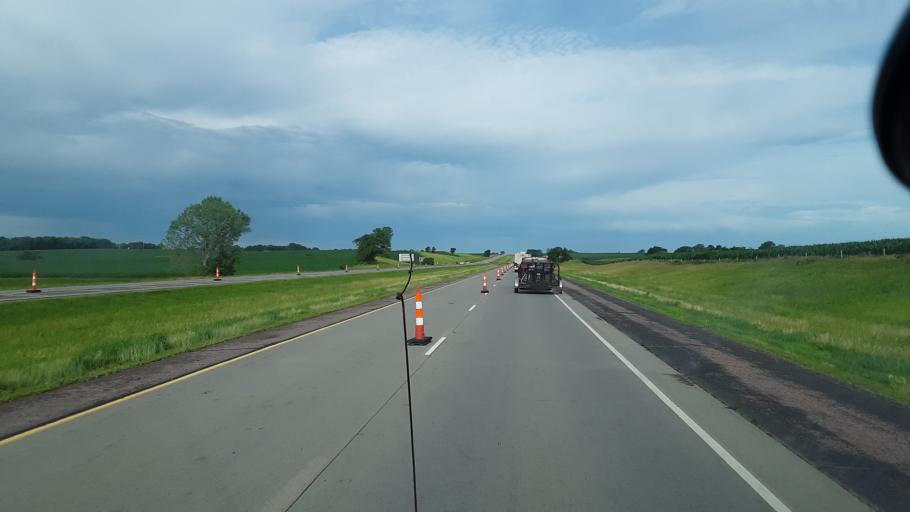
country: US
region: South Dakota
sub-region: Minnehaha County
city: Crooks
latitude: 43.6087
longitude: -96.8357
